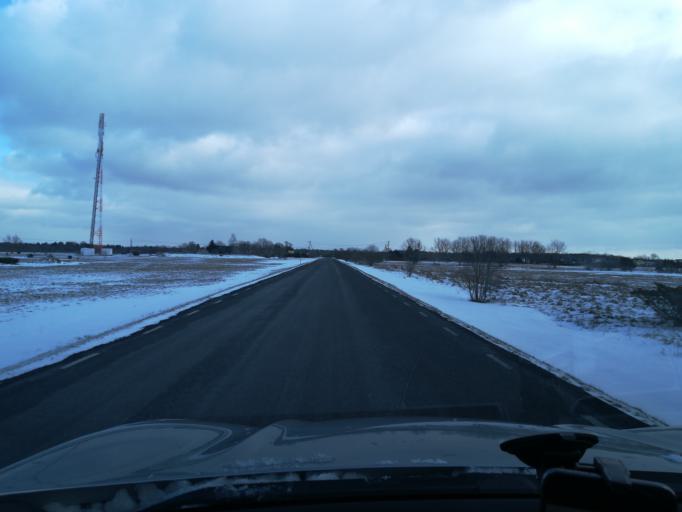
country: EE
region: Harju
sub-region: Harku vald
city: Tabasalu
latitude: 59.4296
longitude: 24.4094
